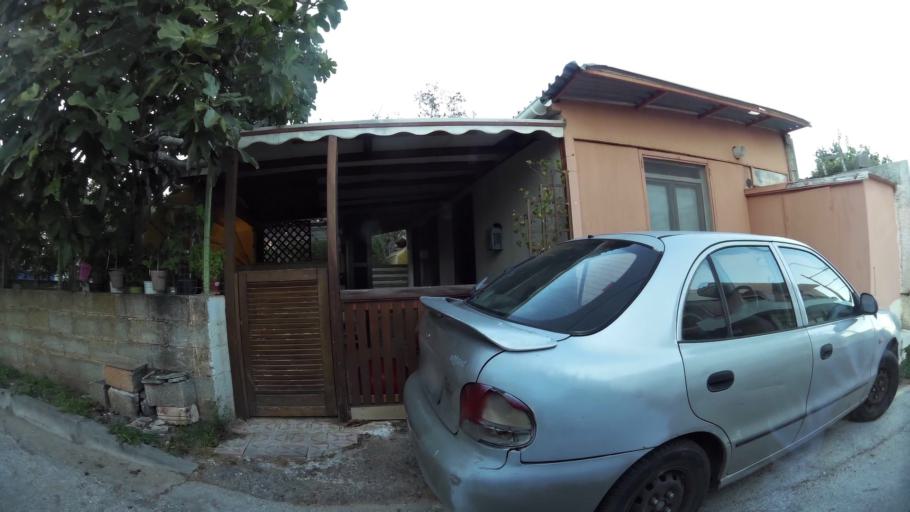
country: GR
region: Attica
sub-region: Nomarchia Anatolikis Attikis
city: Paiania
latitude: 37.9554
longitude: 23.8459
